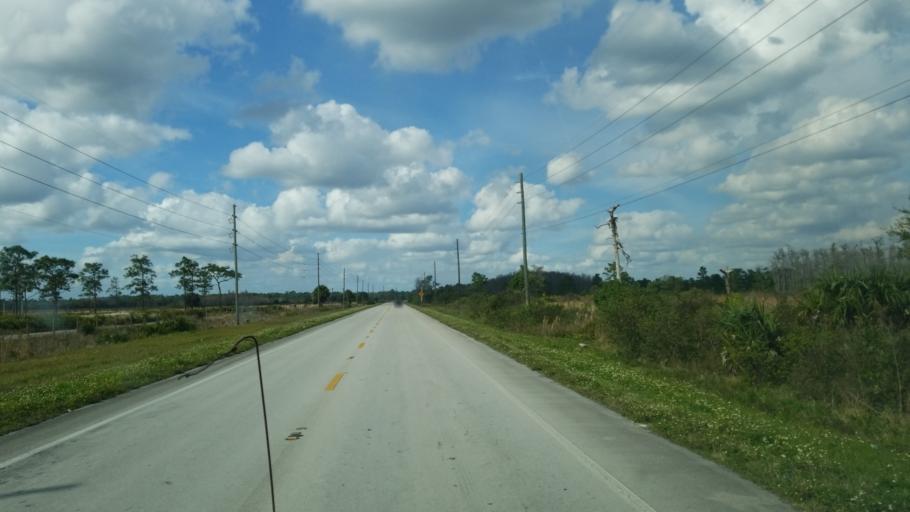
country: US
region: Florida
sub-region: Osceola County
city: Saint Cloud
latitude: 28.0690
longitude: -81.0656
